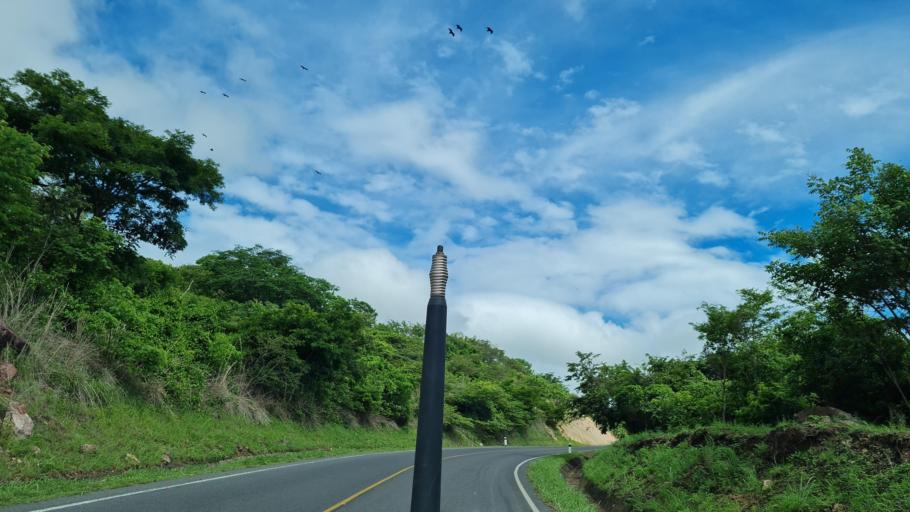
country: NI
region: Boaco
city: San Jose de los Remates
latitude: 12.6109
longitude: -85.8896
